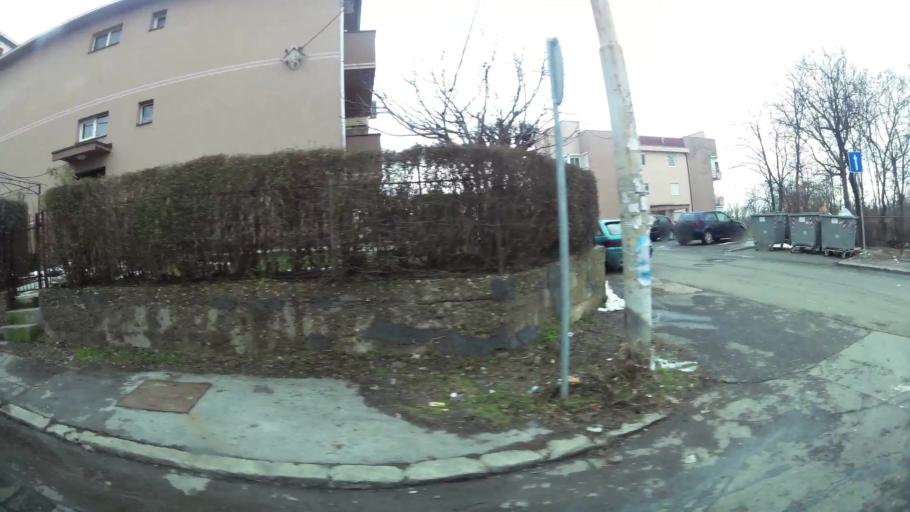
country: RS
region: Central Serbia
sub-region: Belgrade
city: Cukarica
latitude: 44.7527
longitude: 20.4040
